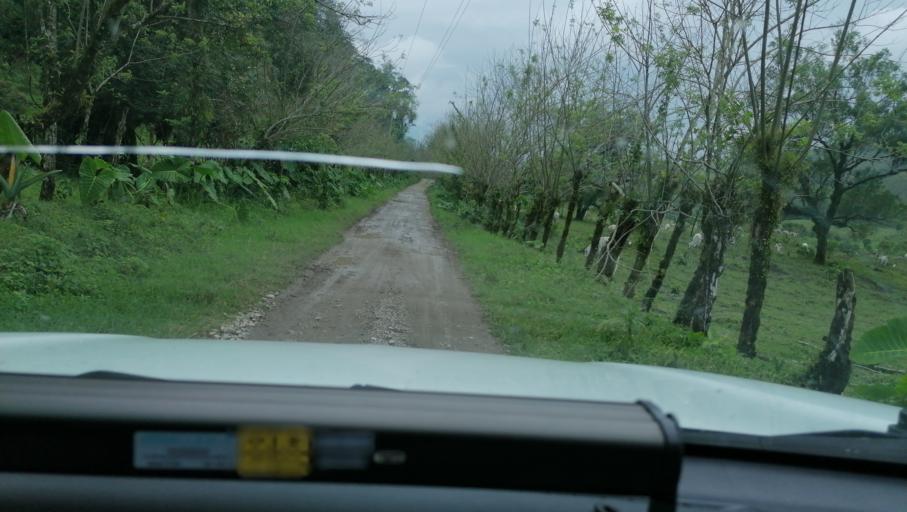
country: MX
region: Chiapas
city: Ixtacomitan
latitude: 17.3525
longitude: -93.1616
